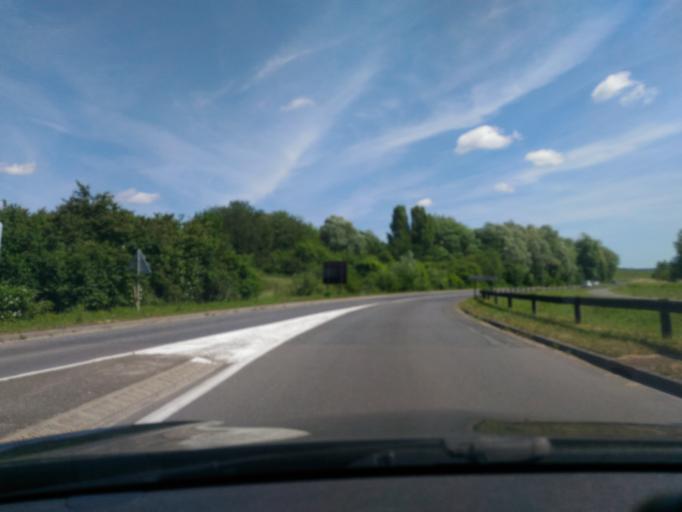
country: FR
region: Ile-de-France
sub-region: Departement de Seine-et-Marne
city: Lieusaint
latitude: 48.6333
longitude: 2.5732
